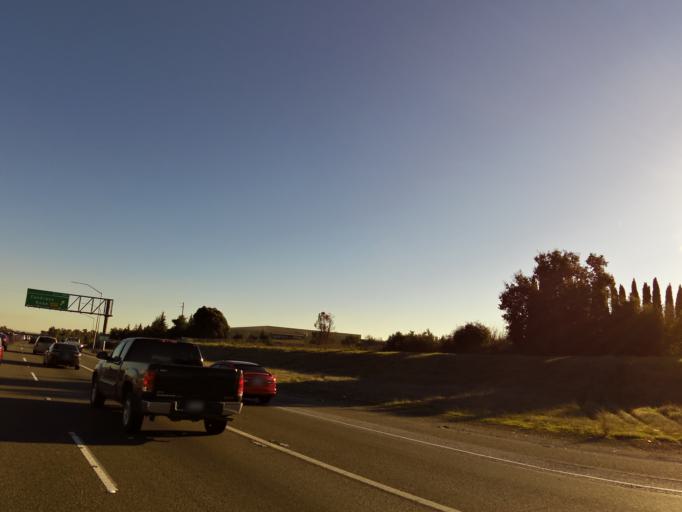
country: US
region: California
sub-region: Santa Clara County
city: Morgan Hill
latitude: 37.1582
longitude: -121.6578
